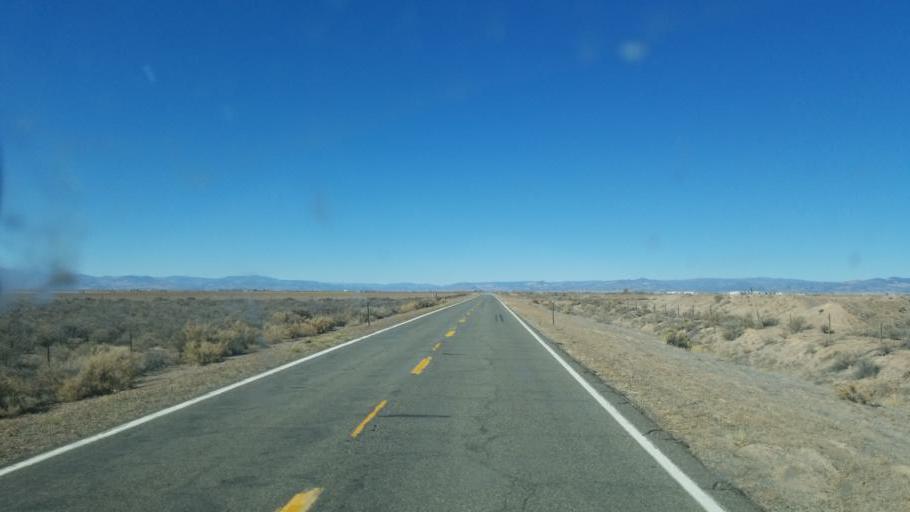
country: US
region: Colorado
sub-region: Saguache County
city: Center
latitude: 37.7488
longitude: -105.9628
